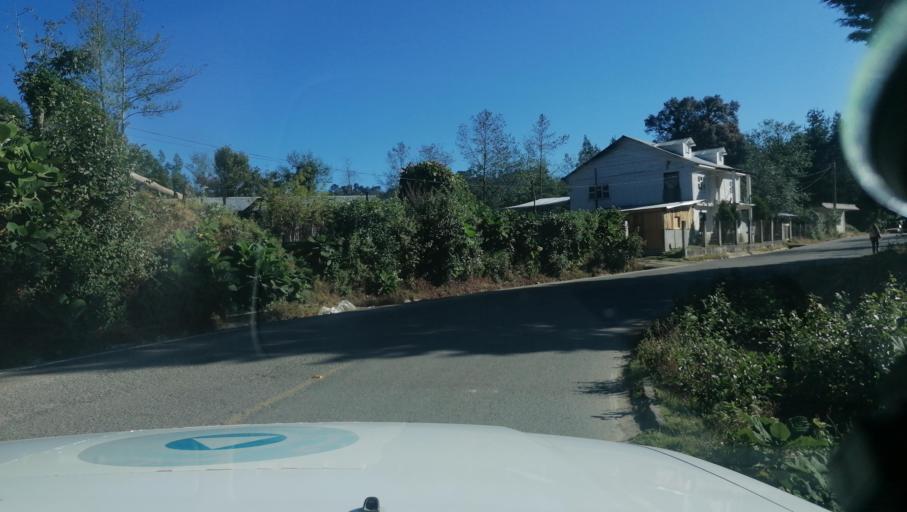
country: MX
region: Chiapas
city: Motozintla de Mendoza
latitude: 15.2523
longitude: -92.2211
